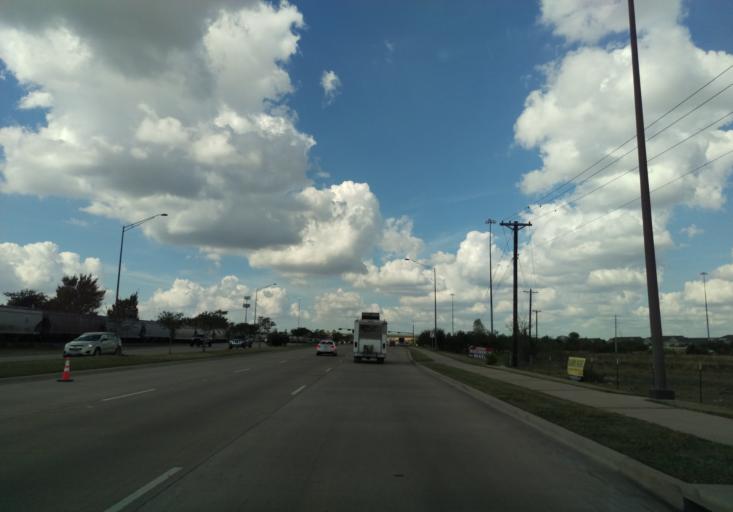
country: US
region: Texas
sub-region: Brazos County
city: College Station
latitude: 30.5833
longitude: -96.3245
